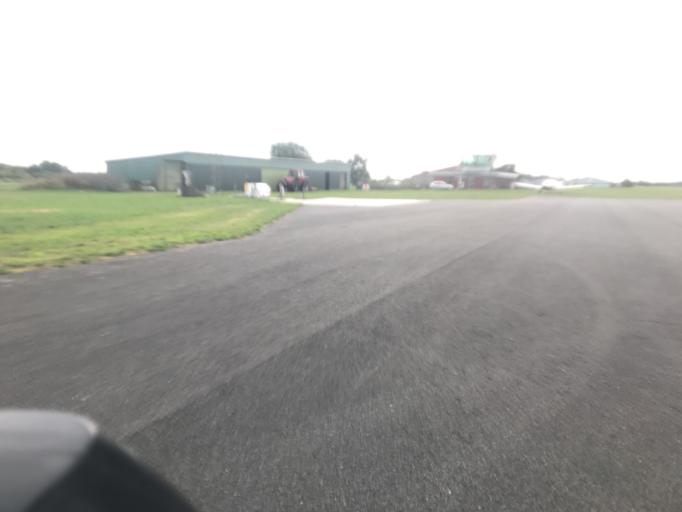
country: DK
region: Central Jutland
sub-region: Herning Kommune
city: Sunds
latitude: 56.1829
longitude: 9.0415
